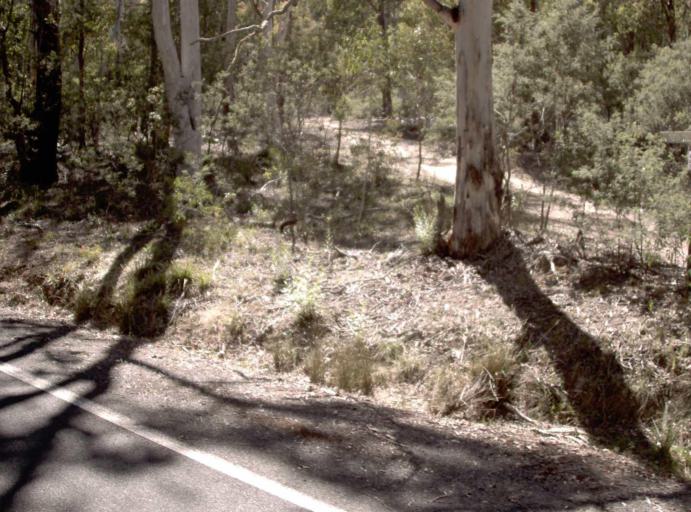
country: AU
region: New South Wales
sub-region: Bombala
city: Bombala
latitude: -37.1252
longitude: 148.7498
